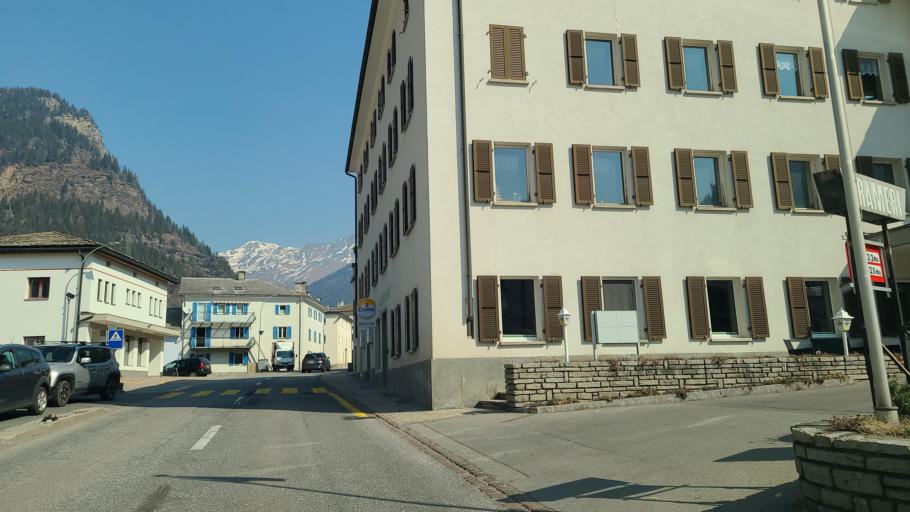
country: CH
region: Grisons
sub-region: Bernina District
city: Poschiavo
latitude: 46.3414
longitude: 10.0600
